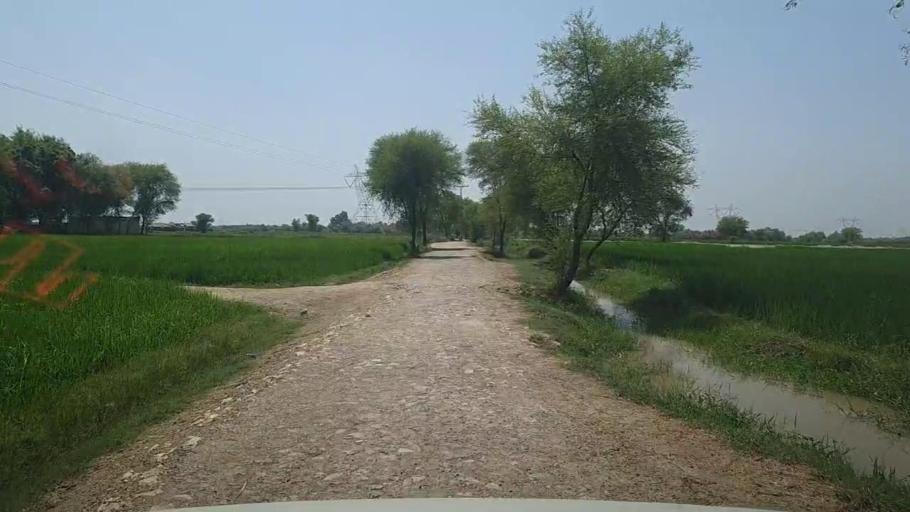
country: PK
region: Sindh
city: Kandhkot
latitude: 28.3162
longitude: 69.3626
